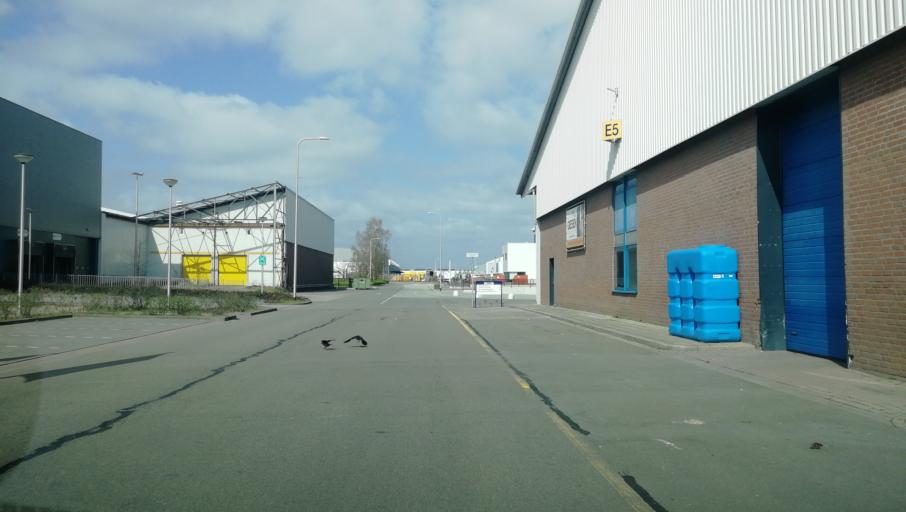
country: NL
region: Limburg
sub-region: Gemeente Venlo
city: Venlo
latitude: 51.4044
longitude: 6.1349
